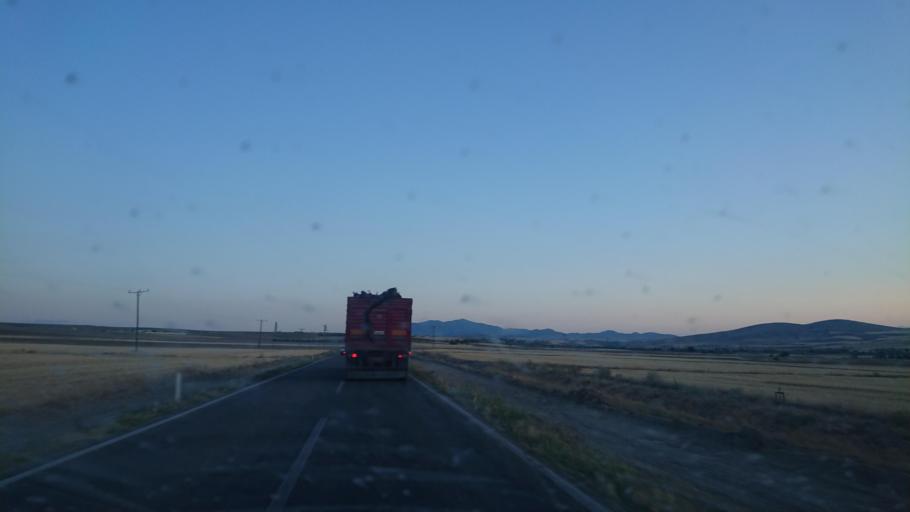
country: TR
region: Aksaray
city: Balci
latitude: 38.8145
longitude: 34.1336
